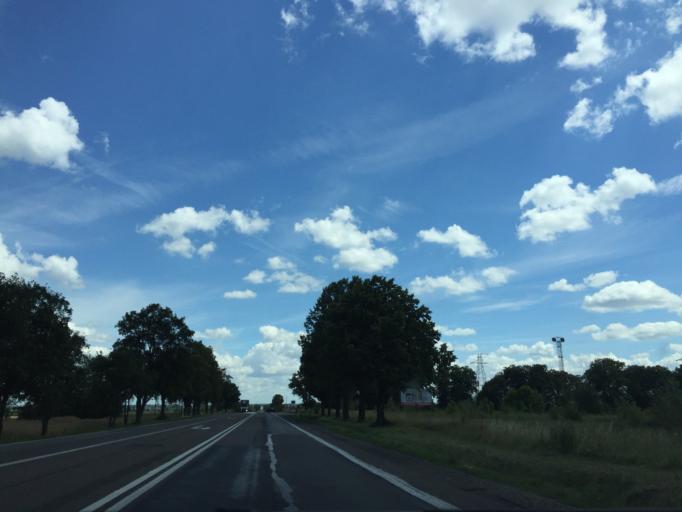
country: PL
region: Lublin Voivodeship
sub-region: Powiat swidnicki
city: Piaski
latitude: 51.1533
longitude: 22.8948
